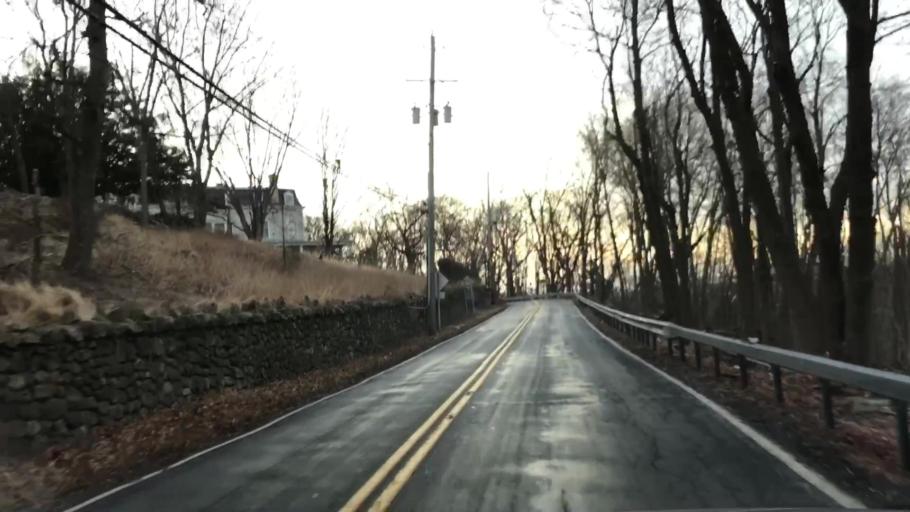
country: US
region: New York
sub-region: Rockland County
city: Stony Point
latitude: 41.2325
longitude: -73.9977
